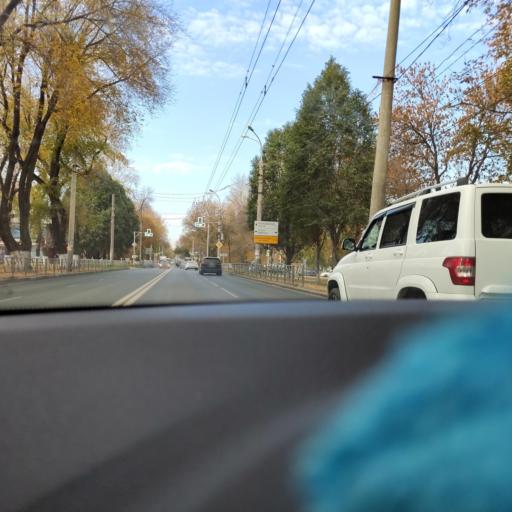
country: RU
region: Samara
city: Samara
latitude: 53.2354
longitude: 50.2424
